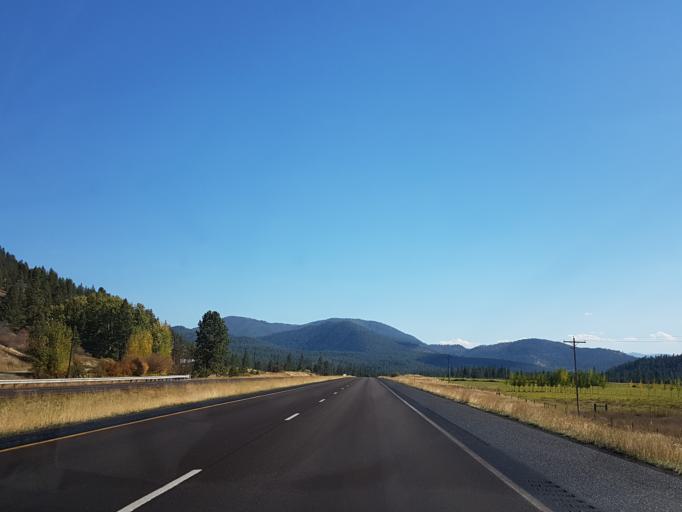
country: US
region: Montana
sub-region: Mineral County
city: Superior
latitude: 47.1410
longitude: -114.8109
